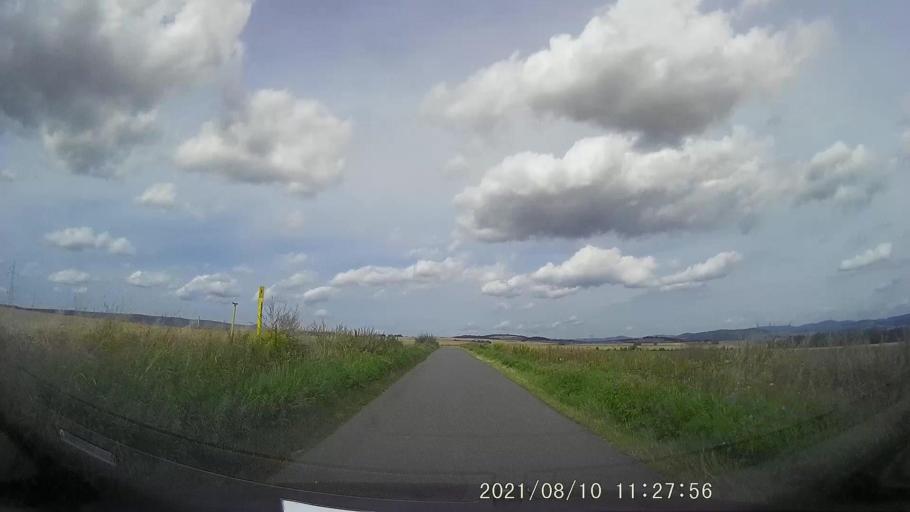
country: PL
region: Lower Silesian Voivodeship
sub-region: Powiat klodzki
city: Bozkow
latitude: 50.4377
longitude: 16.5804
